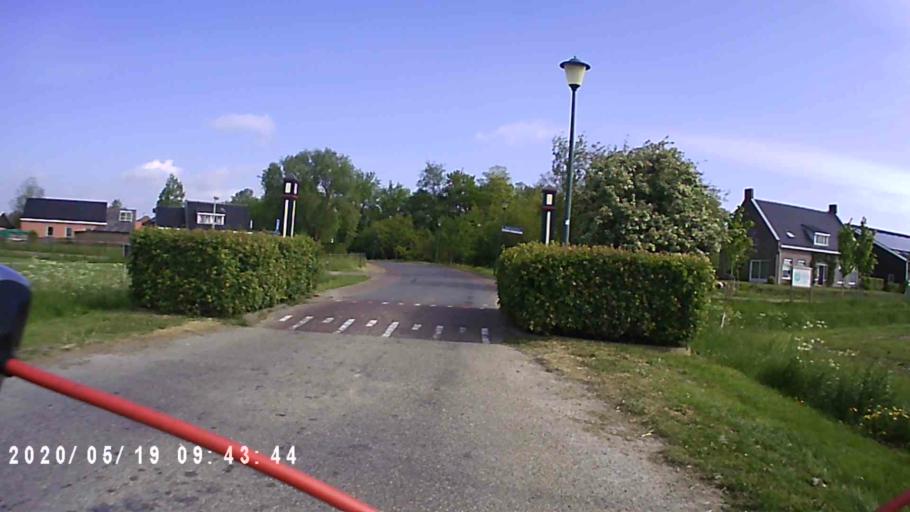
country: NL
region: Groningen
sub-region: Gemeente Zuidhorn
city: Grijpskerk
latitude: 53.2791
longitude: 6.2708
